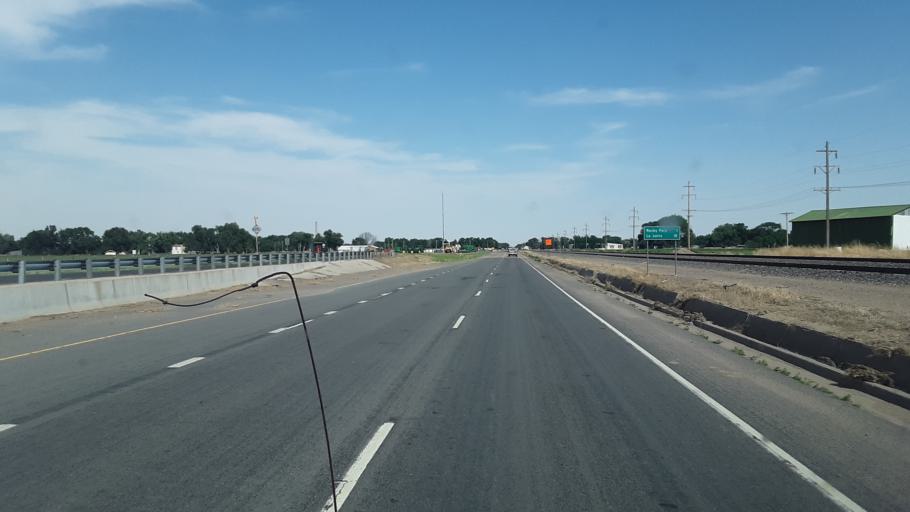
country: US
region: Colorado
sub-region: Otero County
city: Rocky Ford
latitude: 38.0633
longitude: -103.7454
